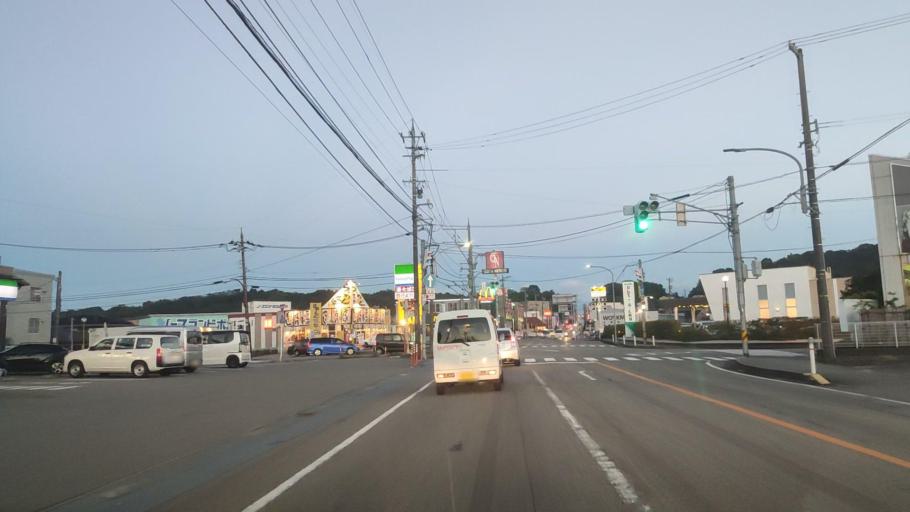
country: JP
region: Toyama
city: Toyama-shi
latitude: 36.7092
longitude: 137.1740
